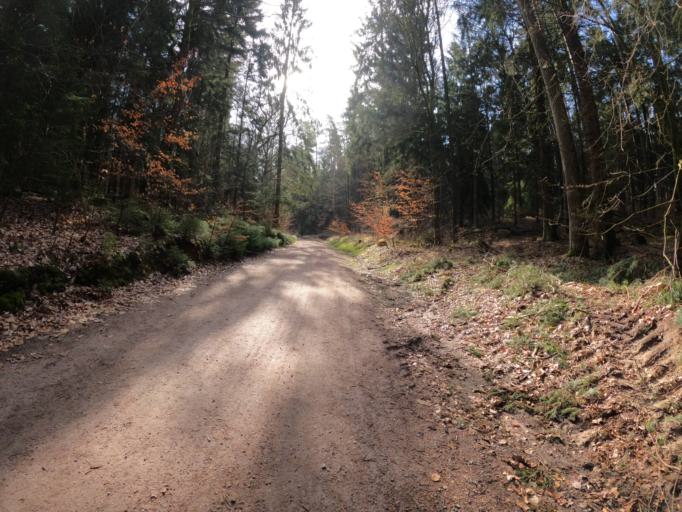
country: DE
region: Lower Saxony
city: Neu Wulmstorf
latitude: 53.4443
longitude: 9.8718
